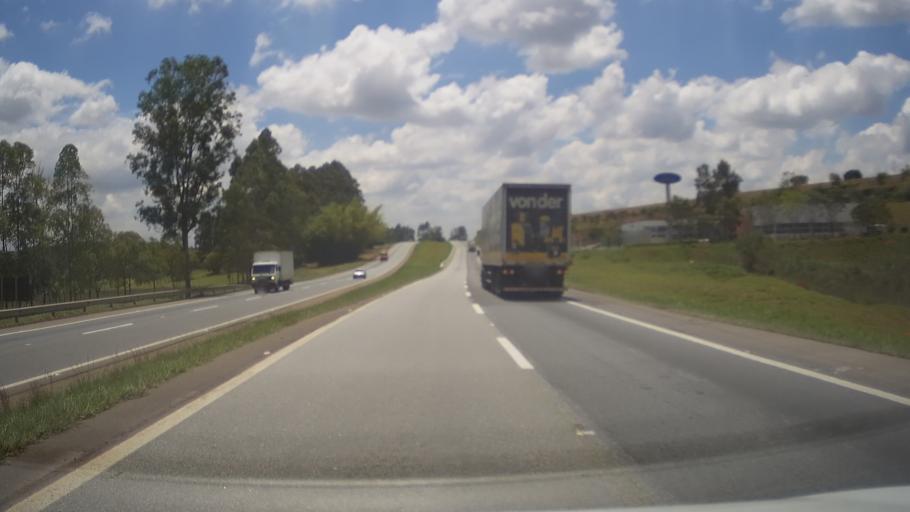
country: BR
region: Minas Gerais
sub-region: Campanha
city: Campanha
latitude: -21.7944
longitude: -45.4523
